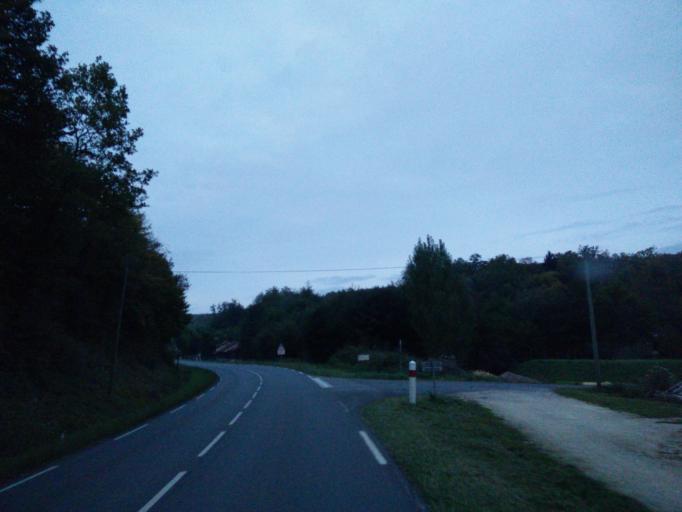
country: FR
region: Aquitaine
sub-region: Departement de la Dordogne
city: Saint-Cyprien
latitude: 44.9105
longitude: 1.1133
